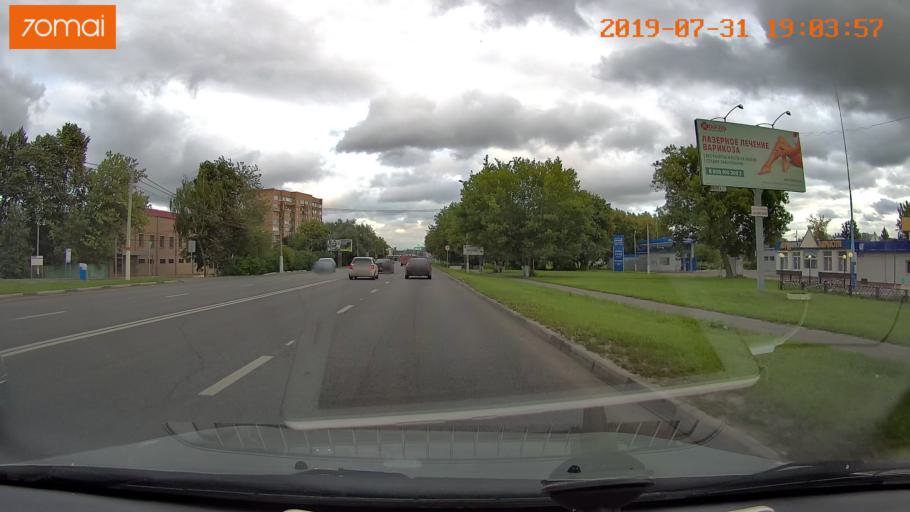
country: RU
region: Moskovskaya
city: Raduzhnyy
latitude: 55.1118
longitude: 38.7388
